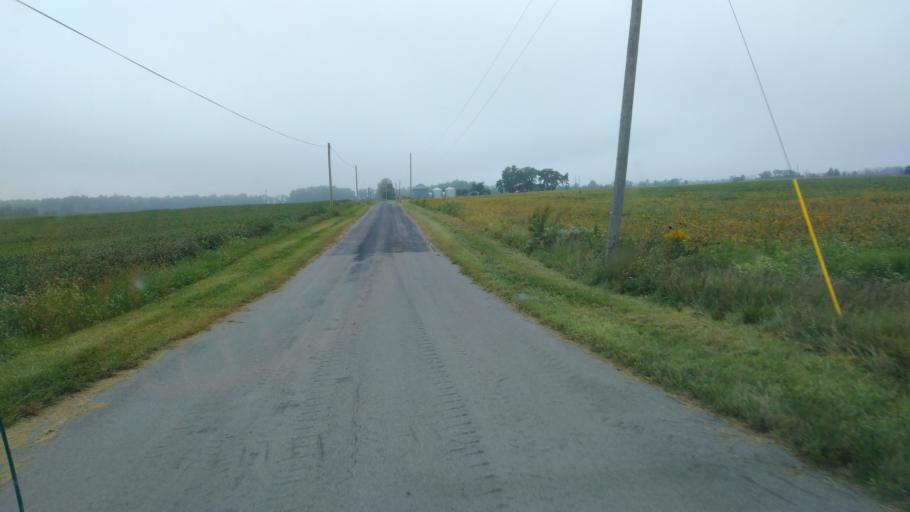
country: US
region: Ohio
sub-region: Hardin County
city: Kenton
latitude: 40.5219
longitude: -83.6009
